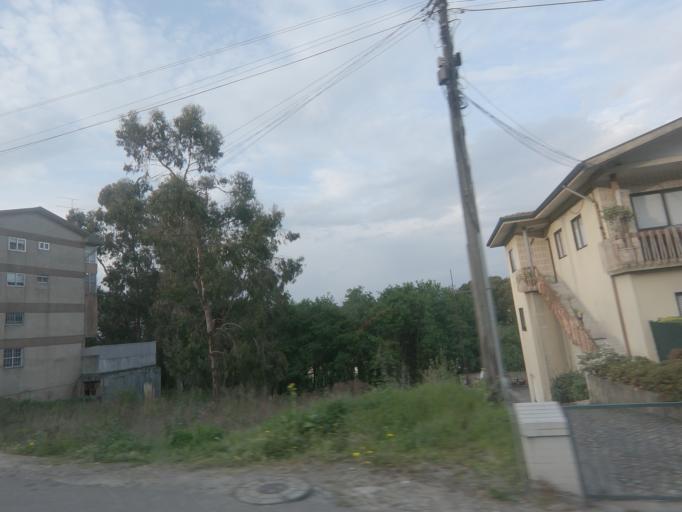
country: PT
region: Porto
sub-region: Valongo
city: Valongo
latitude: 41.1916
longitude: -8.5132
